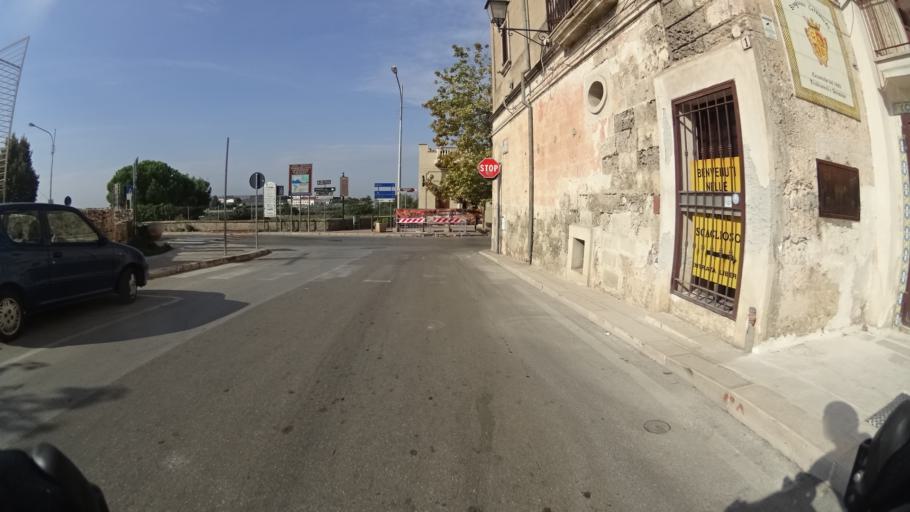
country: IT
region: Apulia
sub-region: Provincia di Taranto
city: Grottaglie
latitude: 40.5319
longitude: 17.4295
